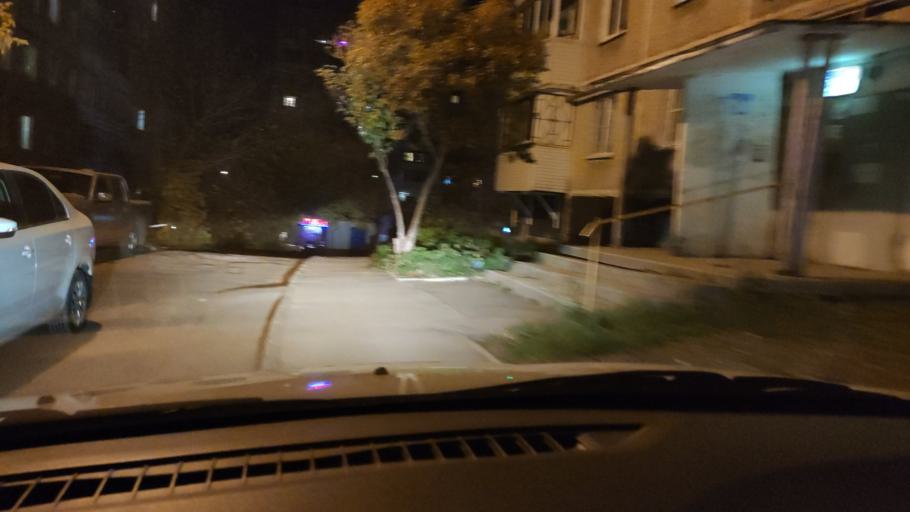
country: RU
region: Perm
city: Perm
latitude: 57.9672
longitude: 56.2165
